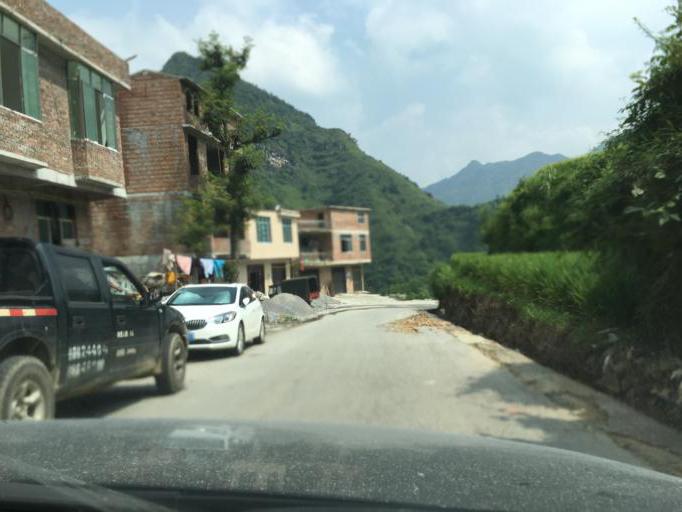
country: CN
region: Guangxi Zhuangzu Zizhiqu
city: Tongle
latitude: 25.2972
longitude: 106.2656
